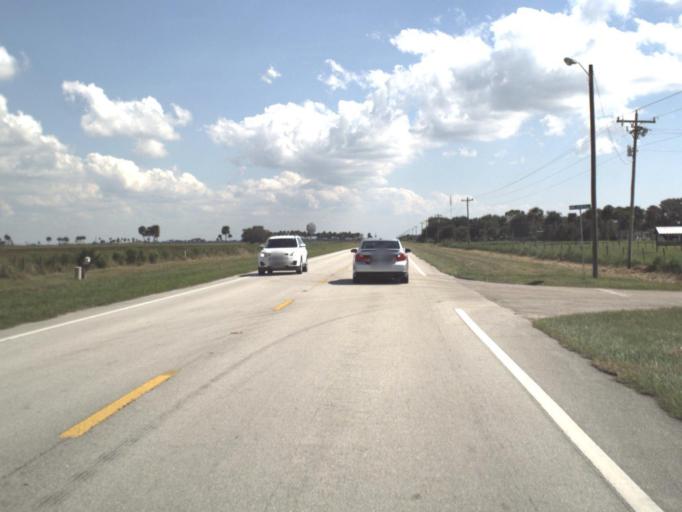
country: US
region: Florida
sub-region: Okeechobee County
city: Okeechobee
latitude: 27.3597
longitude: -80.9641
